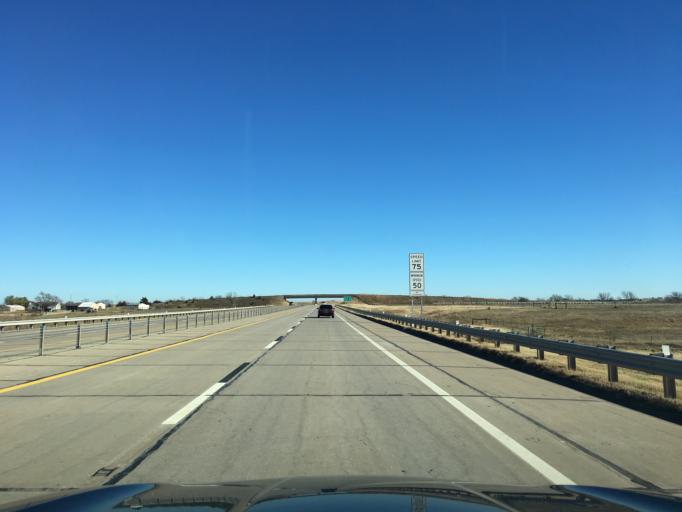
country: US
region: Oklahoma
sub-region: Noble County
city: Perry
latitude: 36.4006
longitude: -97.2696
